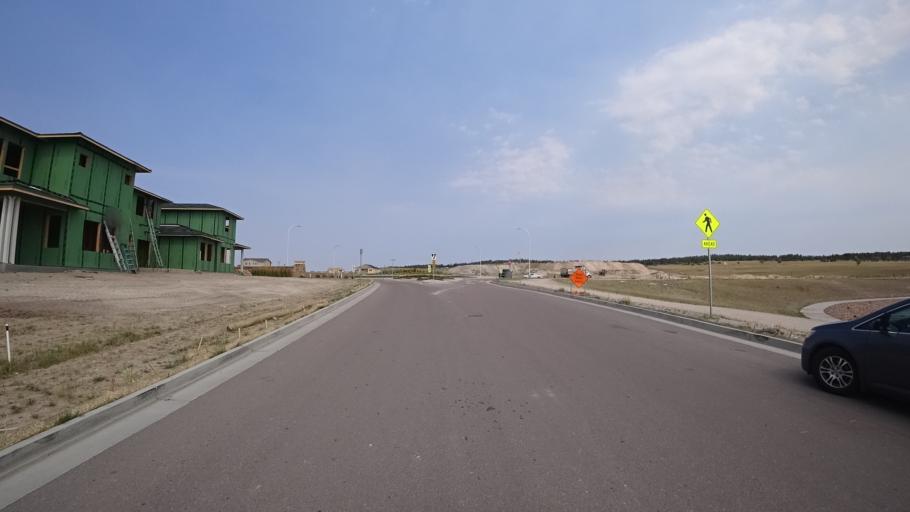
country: US
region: Colorado
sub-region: El Paso County
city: Black Forest
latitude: 38.9748
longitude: -104.7154
